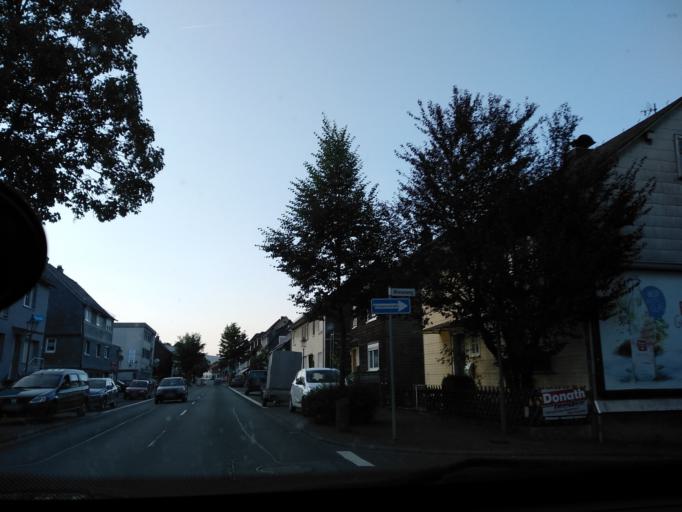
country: DE
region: Hesse
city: Dillenburg
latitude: 50.8113
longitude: 8.3381
